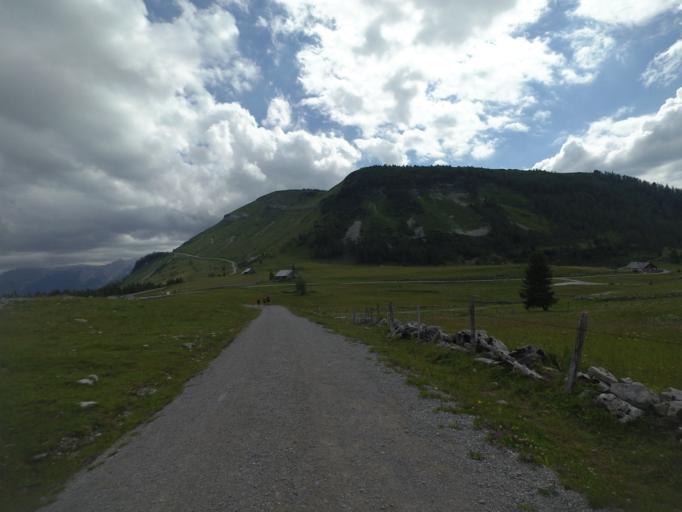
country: AT
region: Salzburg
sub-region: Politischer Bezirk Salzburg-Umgebung
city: Hintersee
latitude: 47.6512
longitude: 13.2823
